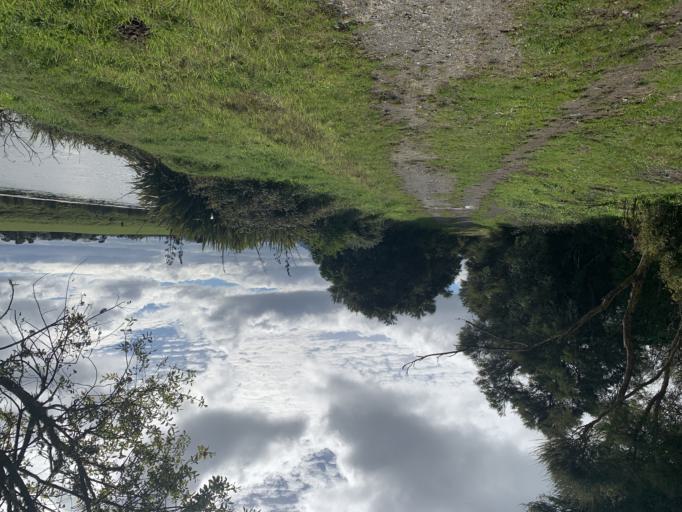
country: NZ
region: Waikato
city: Turangi
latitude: -38.9740
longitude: 175.7774
